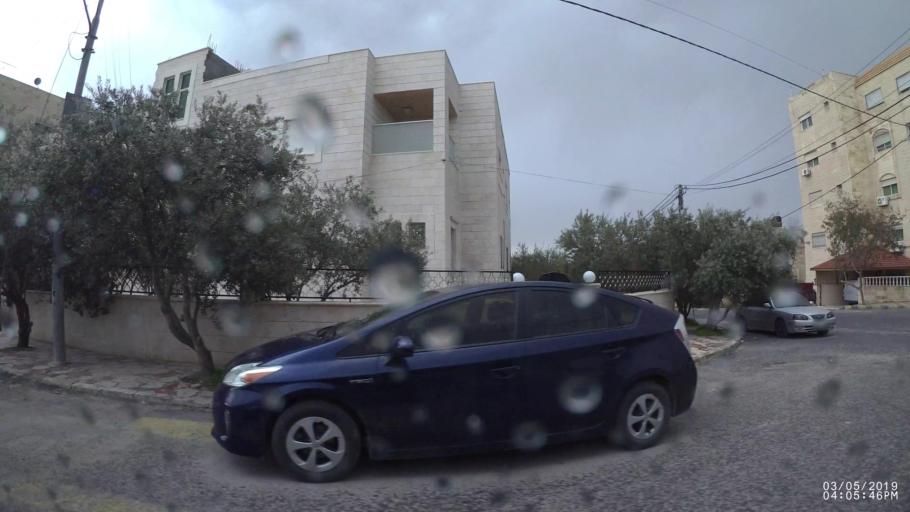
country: JO
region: Amman
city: Amman
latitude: 32.0076
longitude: 35.9561
